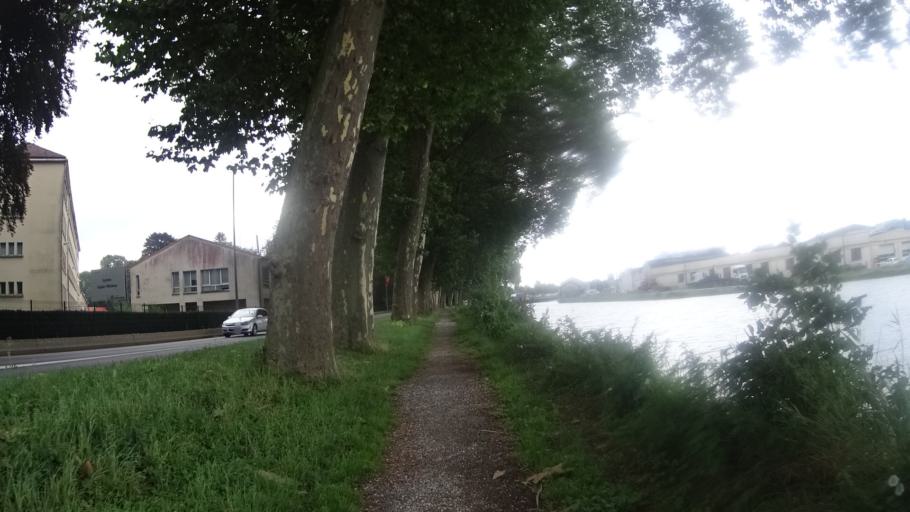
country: FR
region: Lorraine
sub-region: Departement de la Meuse
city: Bar-le-Duc
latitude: 48.7744
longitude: 5.1689
